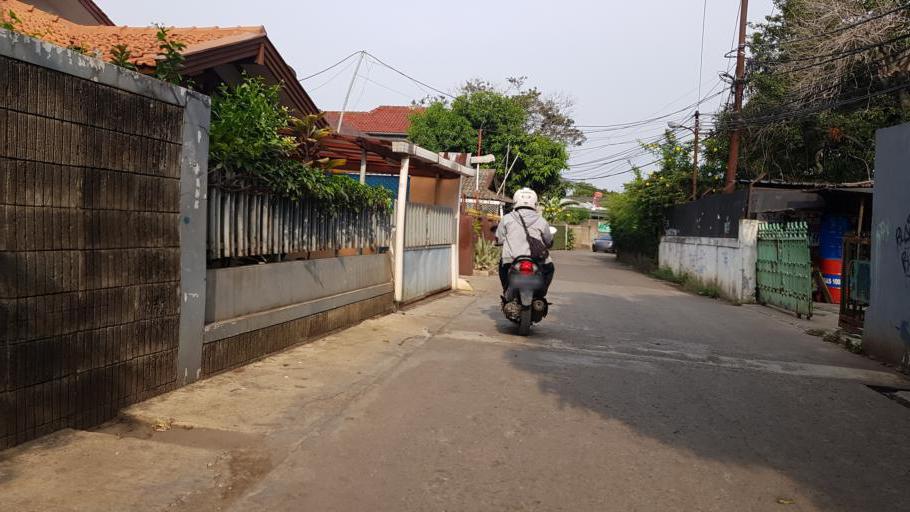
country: ID
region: West Java
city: Pamulang
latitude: -6.3280
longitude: 106.7975
